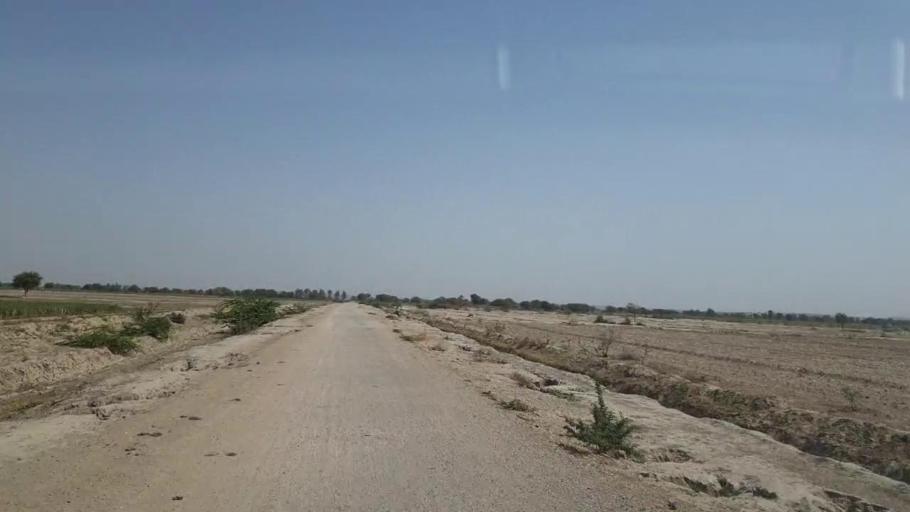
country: PK
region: Sindh
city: Naukot
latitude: 24.9310
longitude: 69.4928
